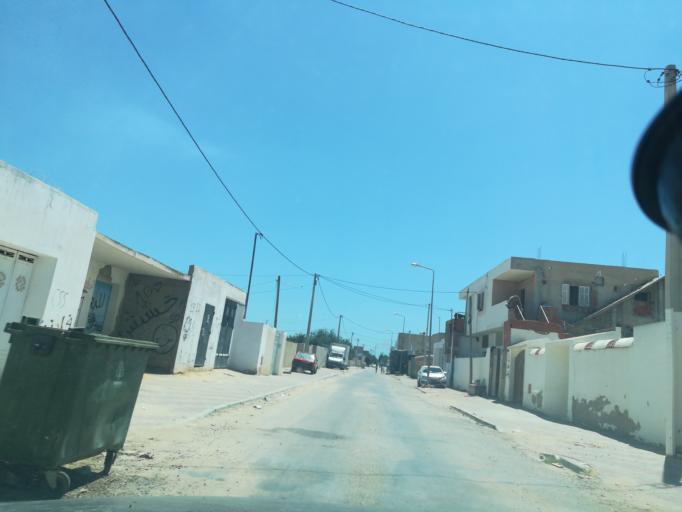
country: TN
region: Safaqis
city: Al Qarmadah
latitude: 34.8243
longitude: 10.7540
